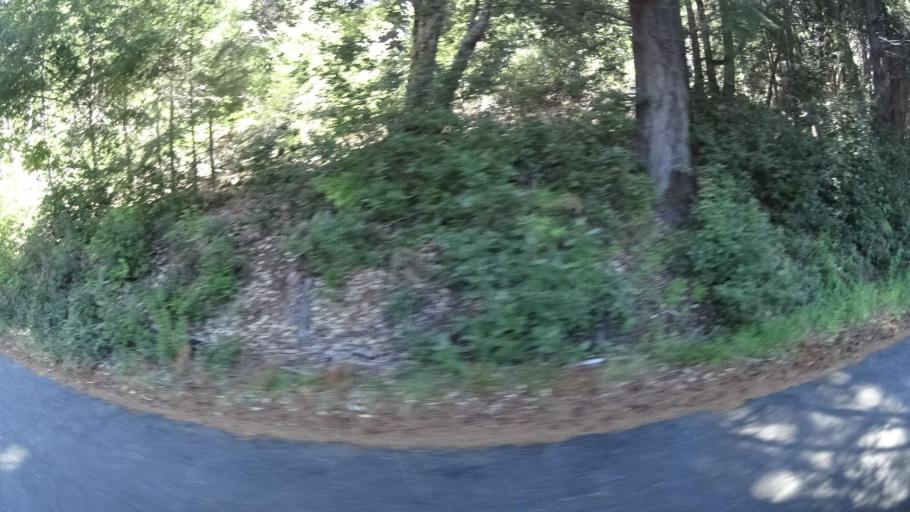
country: US
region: California
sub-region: Humboldt County
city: Redway
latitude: 40.1728
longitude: -124.0886
